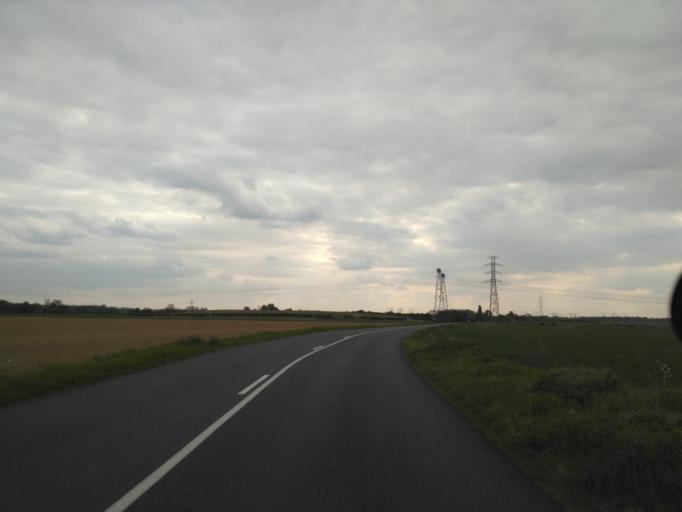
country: FR
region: Ile-de-France
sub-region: Departement de Seine-et-Marne
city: Moisenay
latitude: 48.5720
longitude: 2.7689
